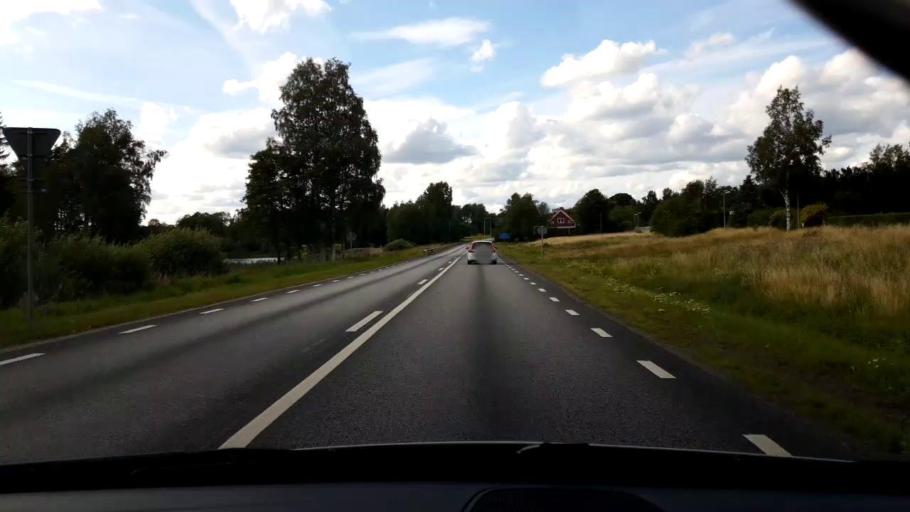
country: SE
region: Joenkoeping
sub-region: Savsjo Kommun
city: Vrigstad
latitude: 57.3586
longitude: 14.4607
